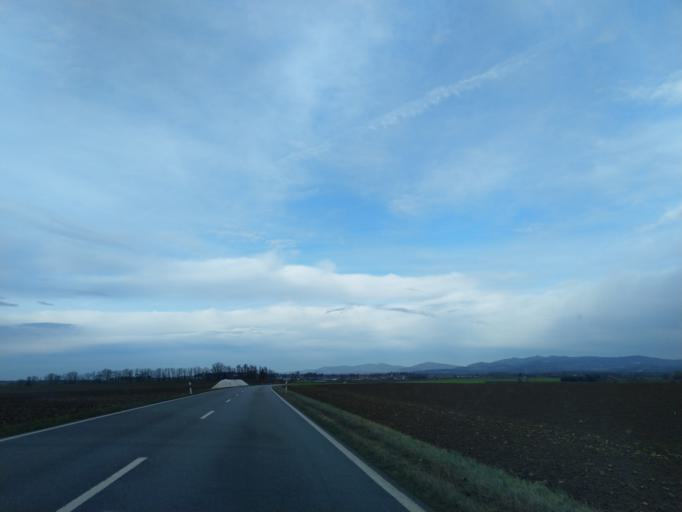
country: DE
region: Bavaria
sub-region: Lower Bavaria
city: Osterhofen
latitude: 48.6704
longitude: 13.0354
